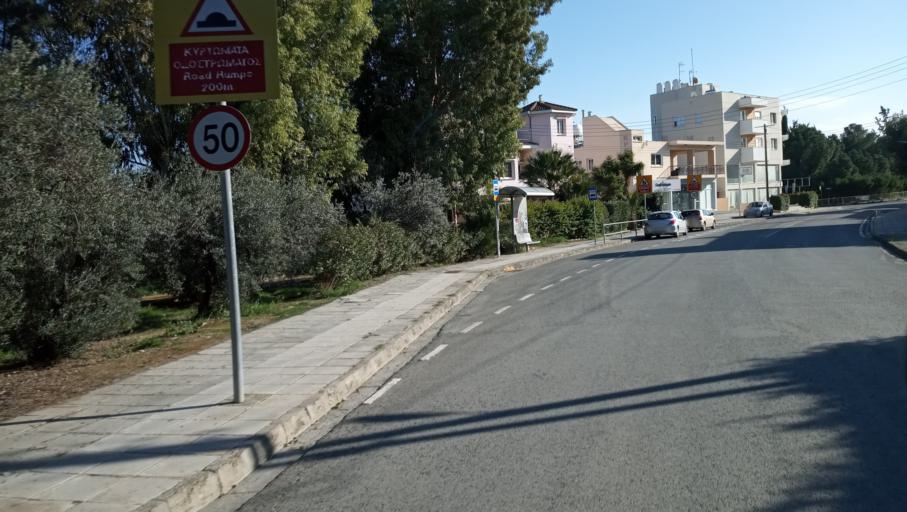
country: CY
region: Lefkosia
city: Nicosia
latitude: 35.1426
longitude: 33.3186
